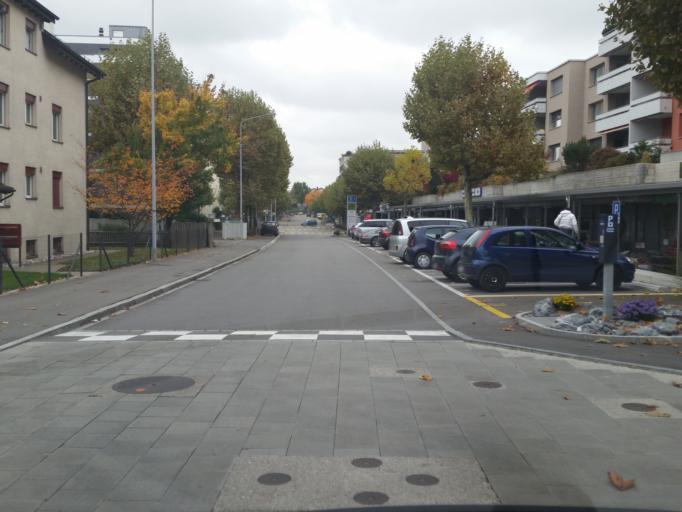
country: CH
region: Zurich
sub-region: Bezirk Dietikon
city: Geroldswil
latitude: 47.4212
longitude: 8.4116
